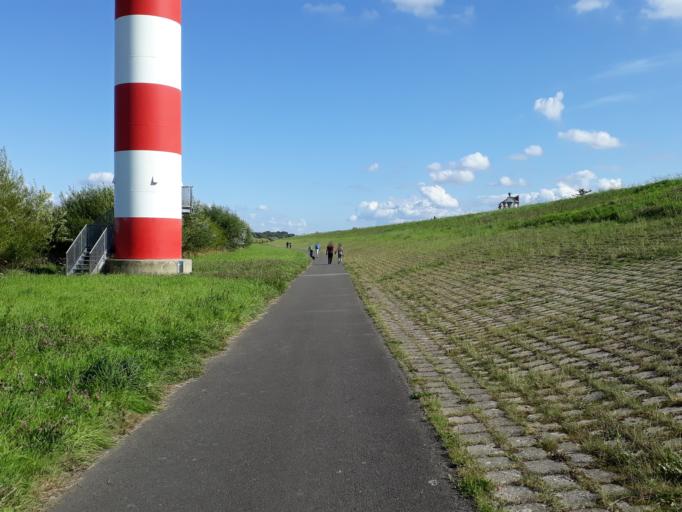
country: DE
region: Lower Saxony
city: Grunendeich
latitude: 53.5696
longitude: 9.6394
